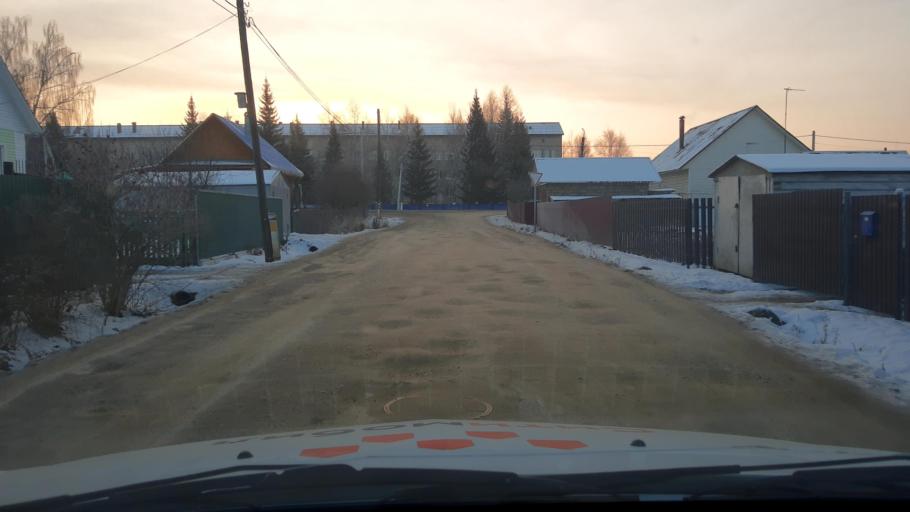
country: RU
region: Bashkortostan
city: Iglino
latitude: 54.8325
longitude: 56.4062
